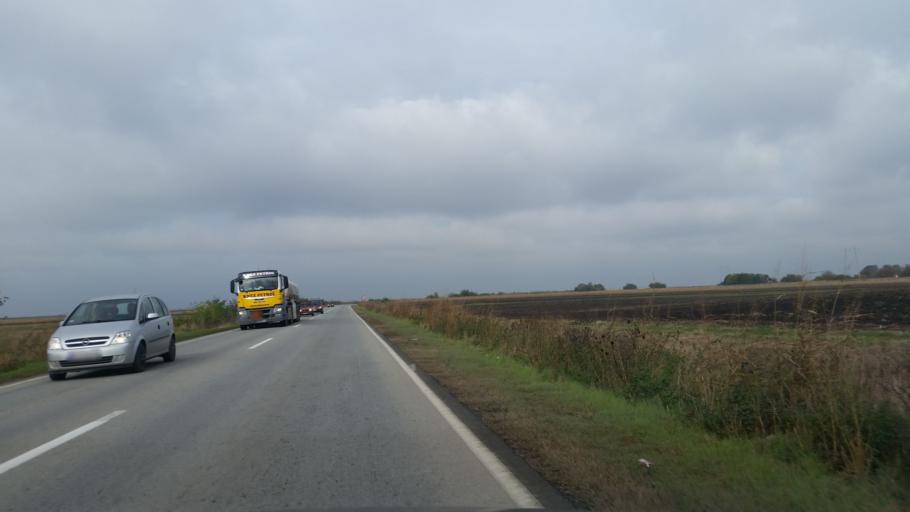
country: RS
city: Elemir
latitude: 45.4624
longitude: 20.3468
